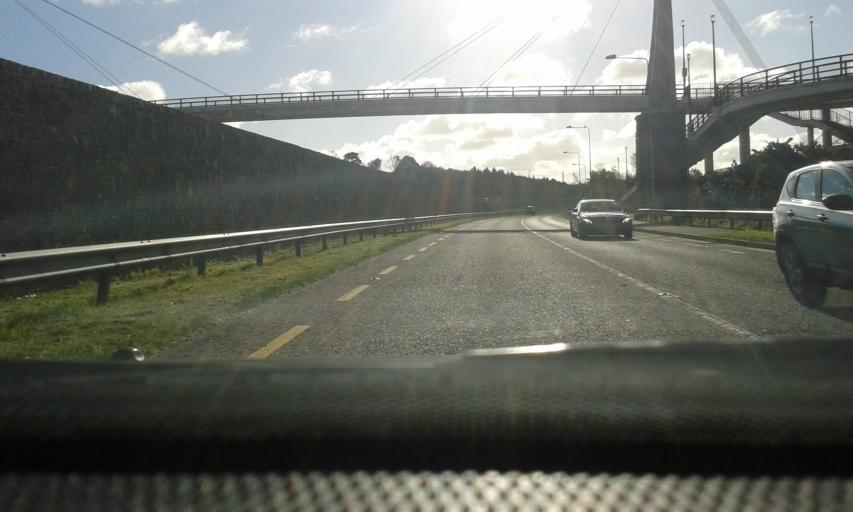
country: IE
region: Munster
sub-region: County Cork
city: Watergrasshill
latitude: 51.9522
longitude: -8.3908
